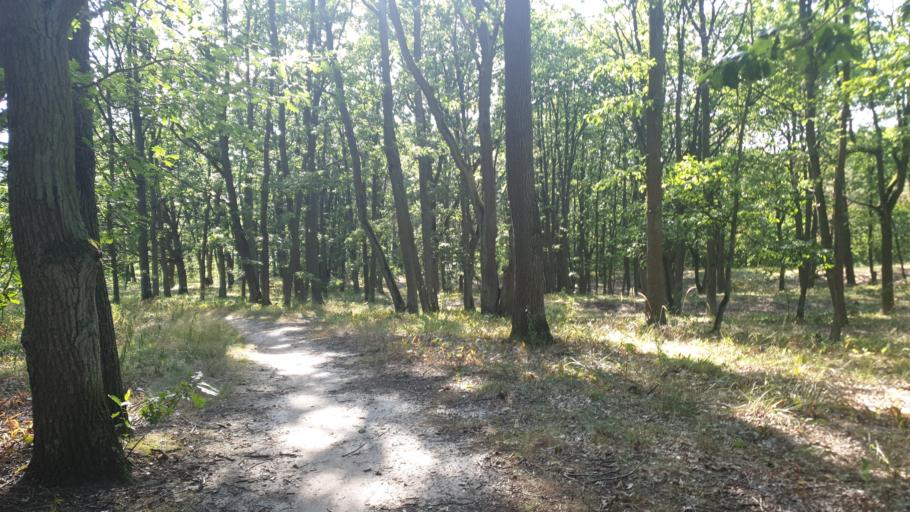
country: PL
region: Kujawsko-Pomorskie
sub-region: Grudziadz
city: Grudziadz
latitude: 53.4577
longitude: 18.7233
